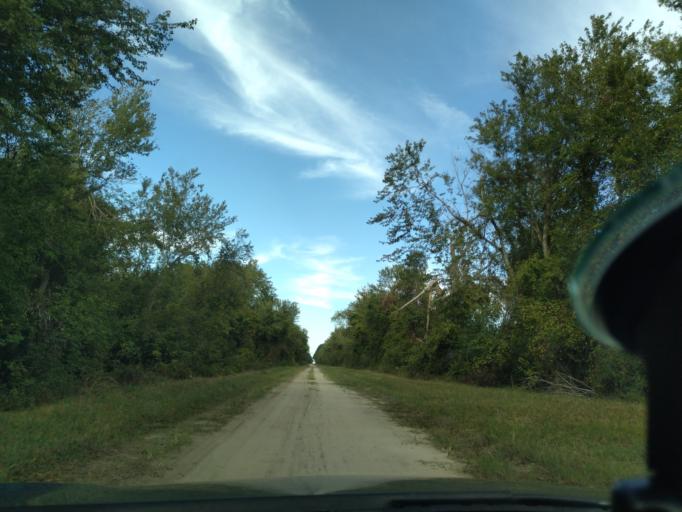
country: US
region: North Carolina
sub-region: Beaufort County
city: Belhaven
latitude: 35.7187
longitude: -76.5807
